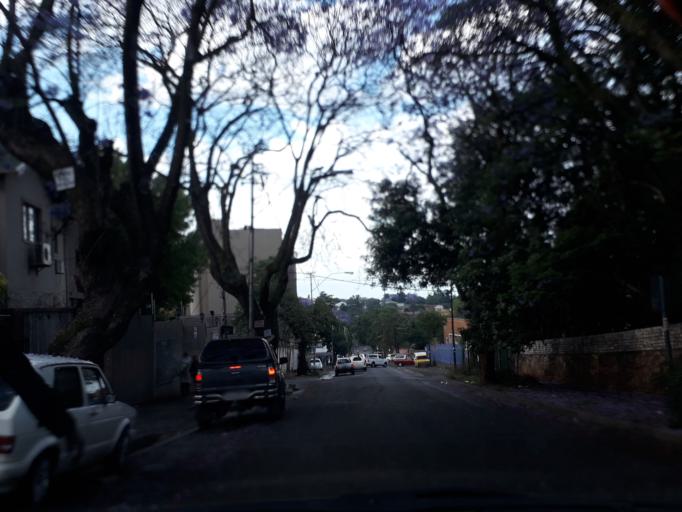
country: ZA
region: Gauteng
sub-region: City of Johannesburg Metropolitan Municipality
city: Johannesburg
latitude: -26.1831
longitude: 28.0717
